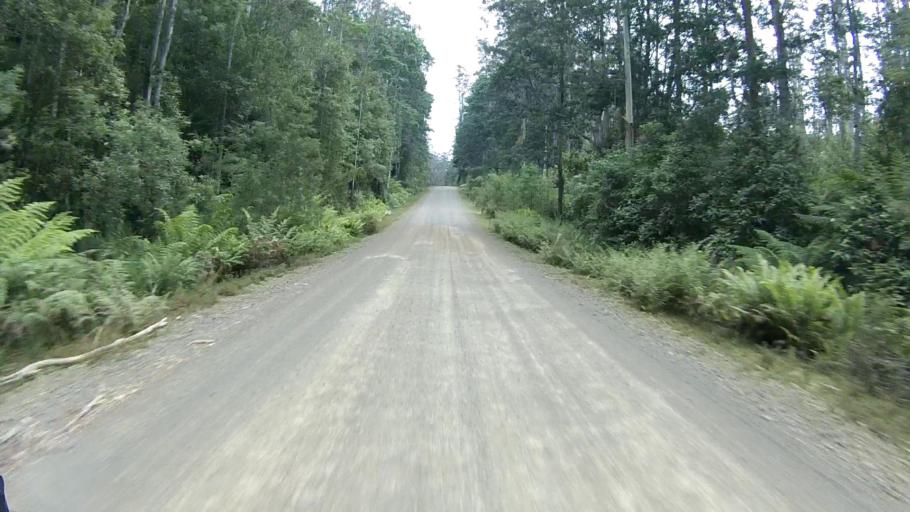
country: AU
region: Tasmania
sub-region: Sorell
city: Sorell
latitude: -42.7159
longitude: 147.8416
